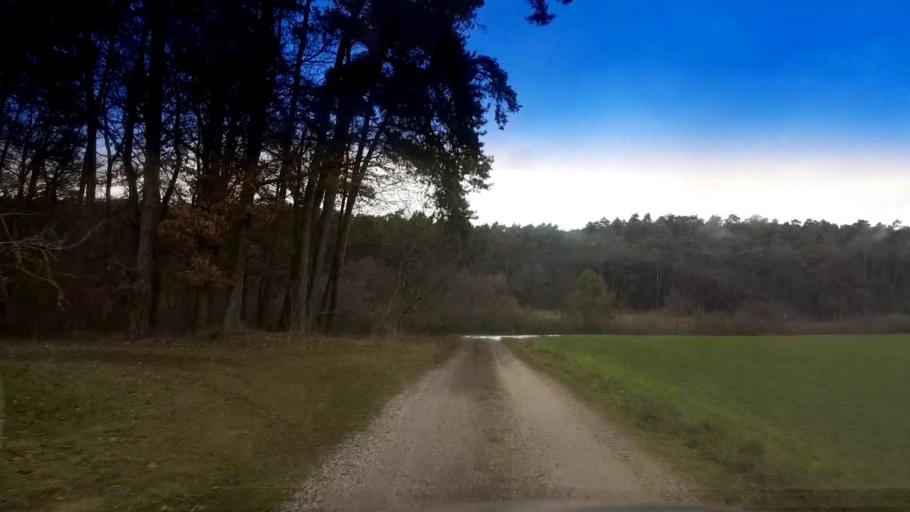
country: DE
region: Bavaria
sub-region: Upper Franconia
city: Lauter
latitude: 49.9550
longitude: 10.7704
